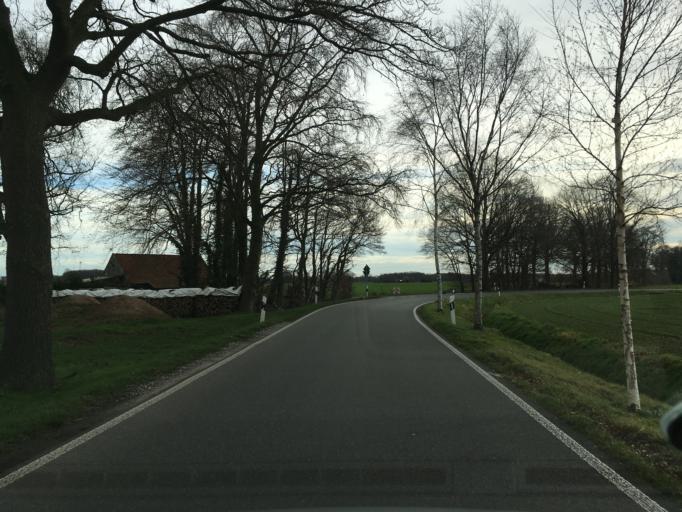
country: DE
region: North Rhine-Westphalia
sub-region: Regierungsbezirk Munster
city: Legden
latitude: 52.0739
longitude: 7.0999
